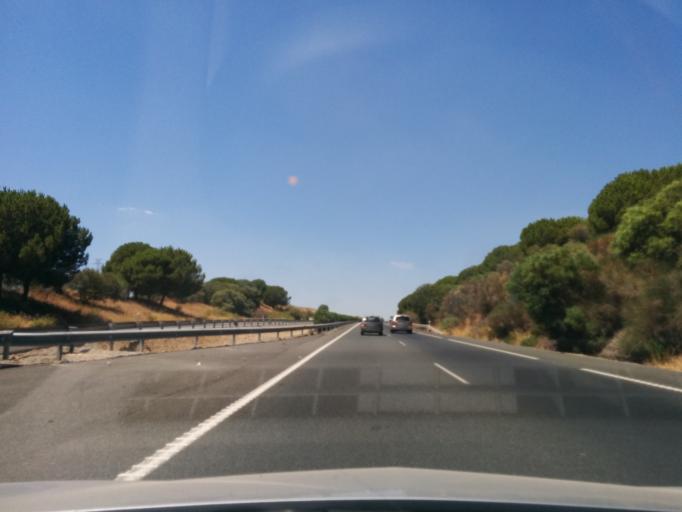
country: ES
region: Andalusia
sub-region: Provincia de Huelva
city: Chucena
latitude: 37.3545
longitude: -6.3615
